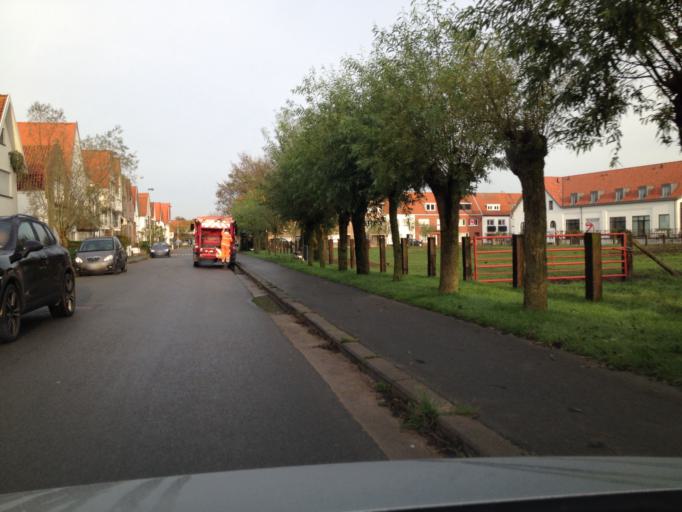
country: BE
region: Flanders
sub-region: Provincie West-Vlaanderen
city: Knokke-Heist
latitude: 51.3477
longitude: 3.3290
